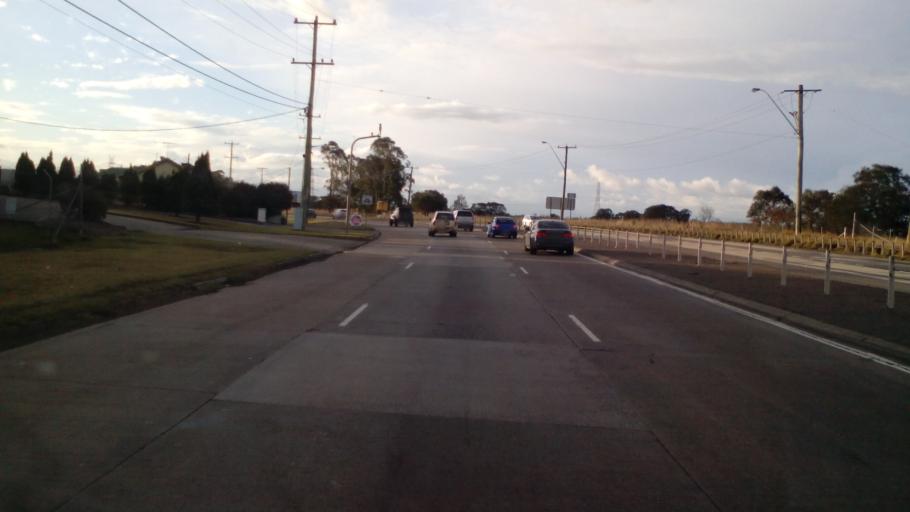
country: AU
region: New South Wales
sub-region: Newcastle
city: Beresfield
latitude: -32.8206
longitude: 151.6819
